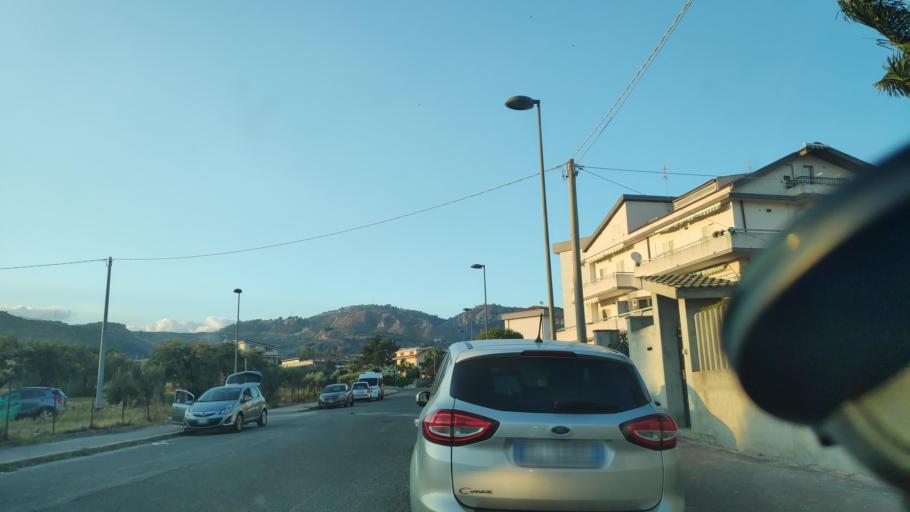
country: IT
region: Calabria
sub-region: Provincia di Reggio Calabria
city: Roccella Ionica
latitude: 38.3188
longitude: 16.3938
